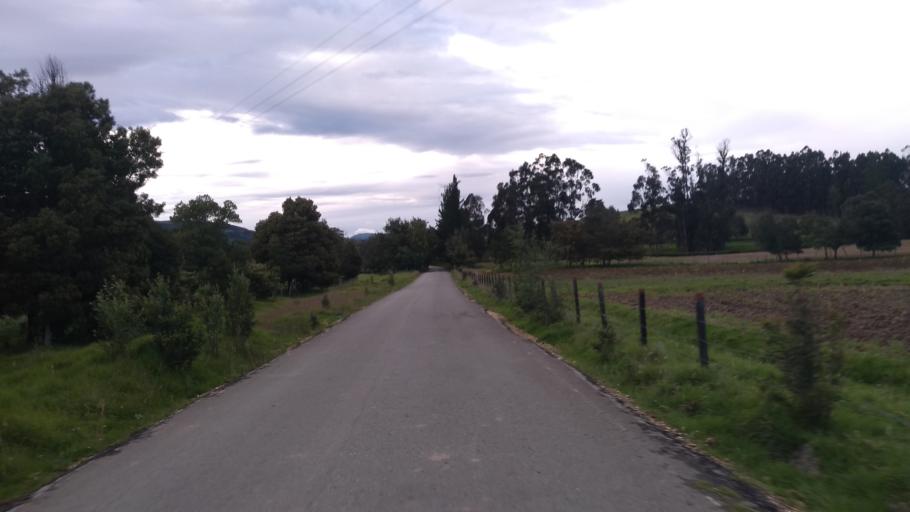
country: CO
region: Boyaca
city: Toca
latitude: 5.5942
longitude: -73.1800
